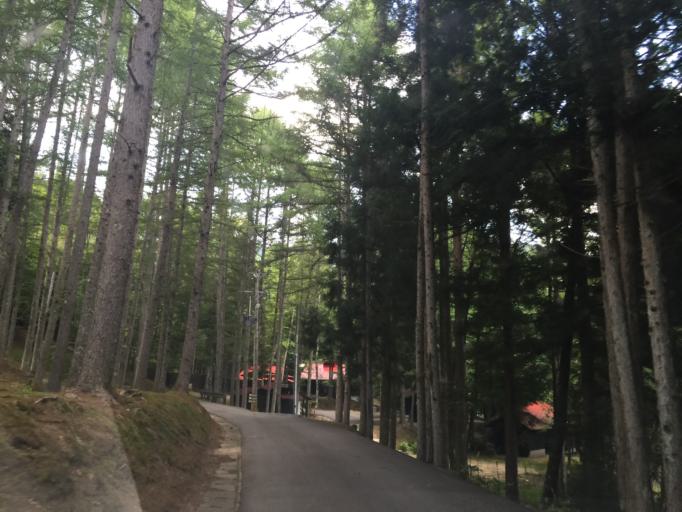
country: JP
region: Nagano
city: Iida
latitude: 35.4037
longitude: 137.6862
